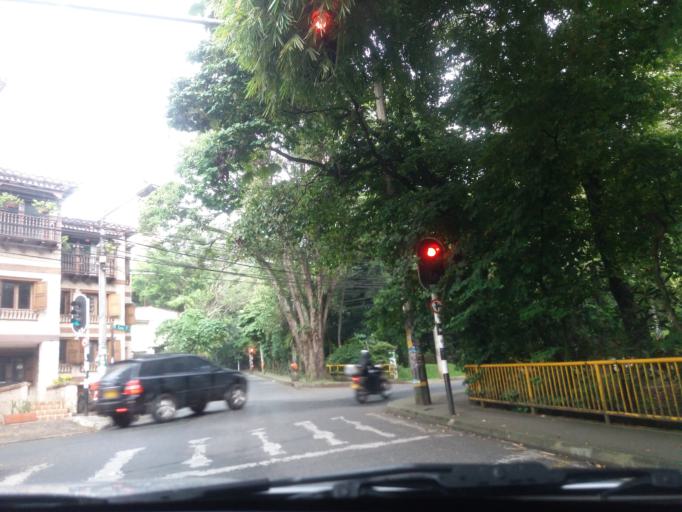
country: CO
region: Antioquia
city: Itagui
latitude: 6.2062
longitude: -75.5654
